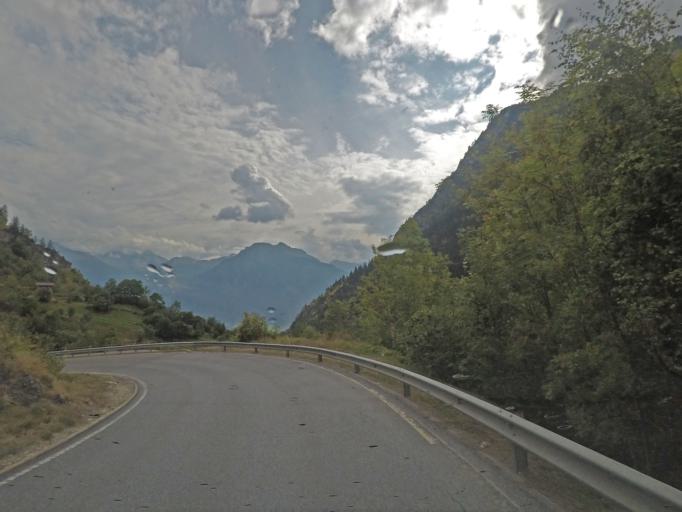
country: CH
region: Valais
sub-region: Brig District
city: Naters
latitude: 46.3546
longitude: 7.9798
